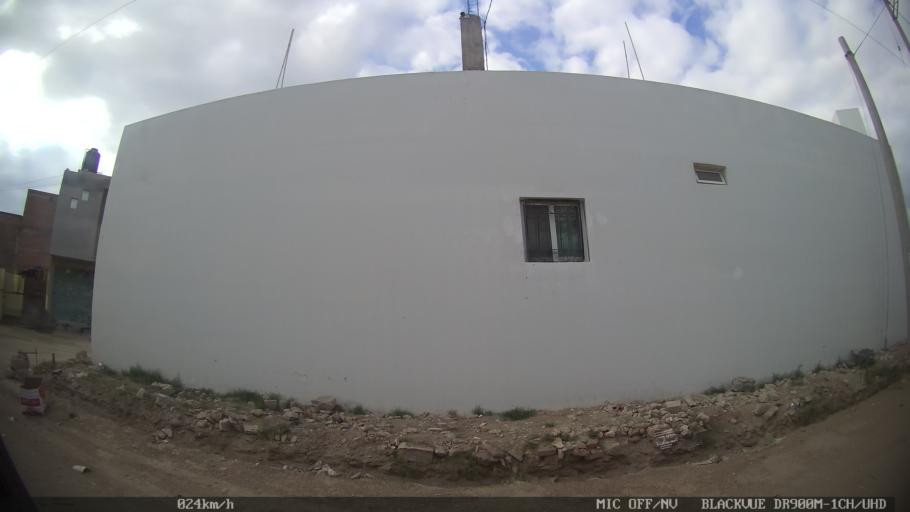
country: MX
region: Jalisco
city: Tonala
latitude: 20.6672
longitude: -103.2386
